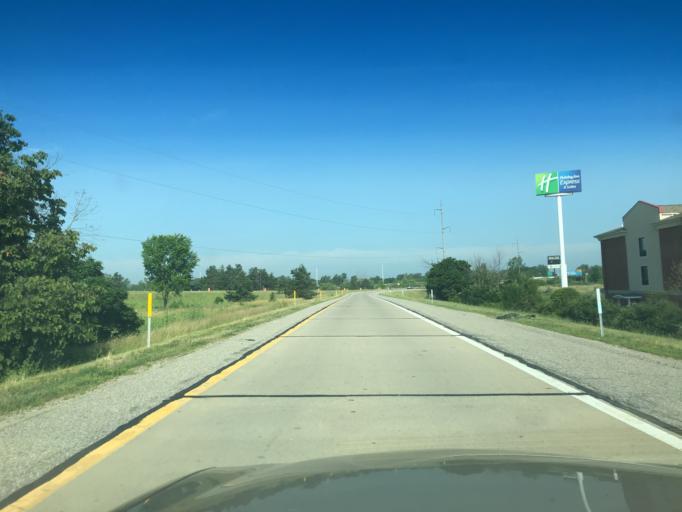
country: US
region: Michigan
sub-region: Eaton County
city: Dimondale
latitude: 42.6795
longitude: -84.6517
